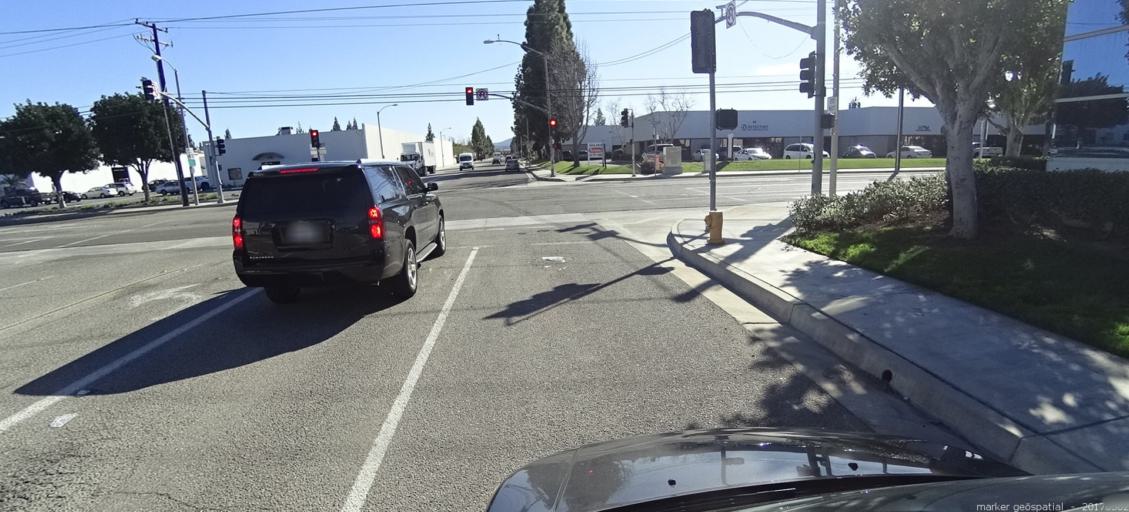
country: US
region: California
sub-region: Orange County
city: Yorba Linda
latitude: 33.8620
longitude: -117.8263
